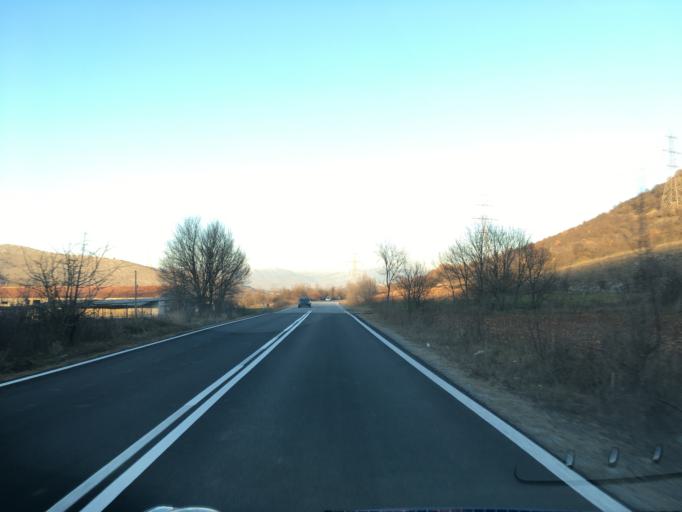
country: GR
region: West Macedonia
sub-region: Nomos Kozanis
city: Kozani
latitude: 40.3171
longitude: 21.7625
